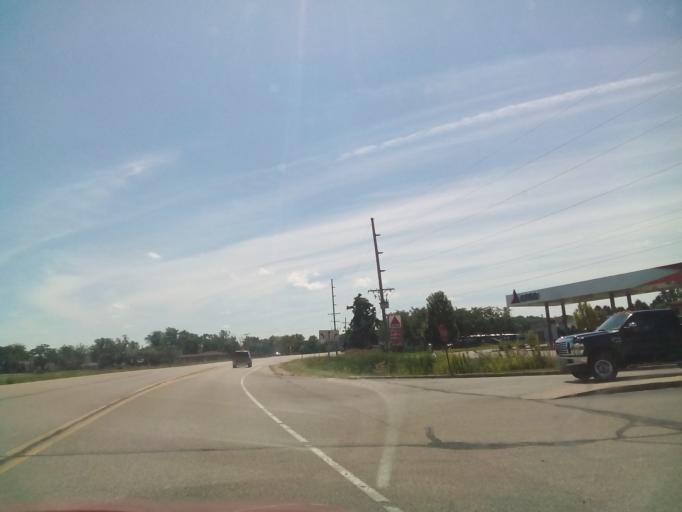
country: US
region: Wisconsin
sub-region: Green County
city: Monticello
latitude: 42.7506
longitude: -89.6022
